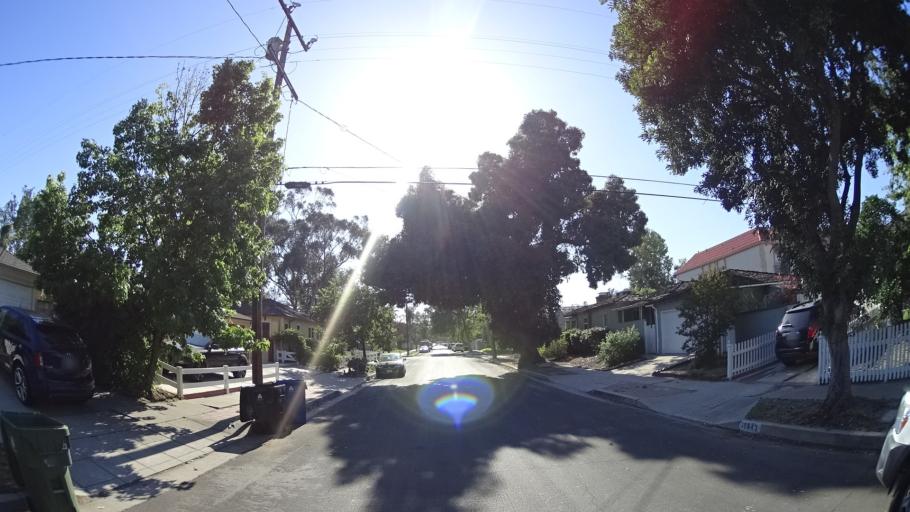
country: US
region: California
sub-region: Los Angeles County
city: Universal City
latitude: 34.1567
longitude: -118.3632
